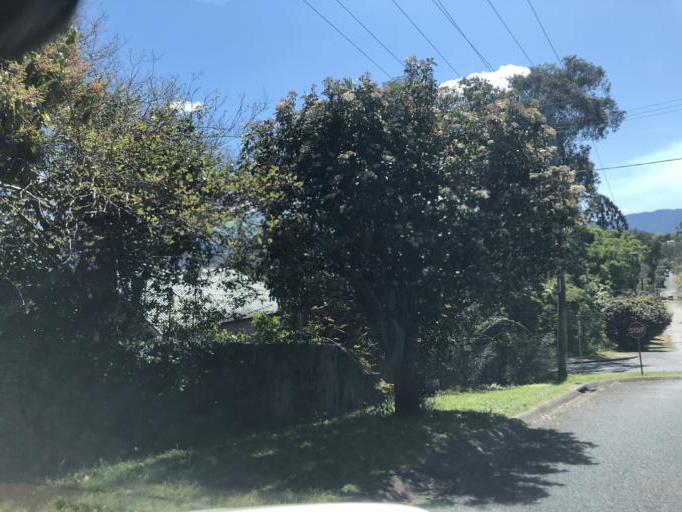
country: AU
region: New South Wales
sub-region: Bellingen
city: Bellingen
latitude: -30.4565
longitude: 152.8984
